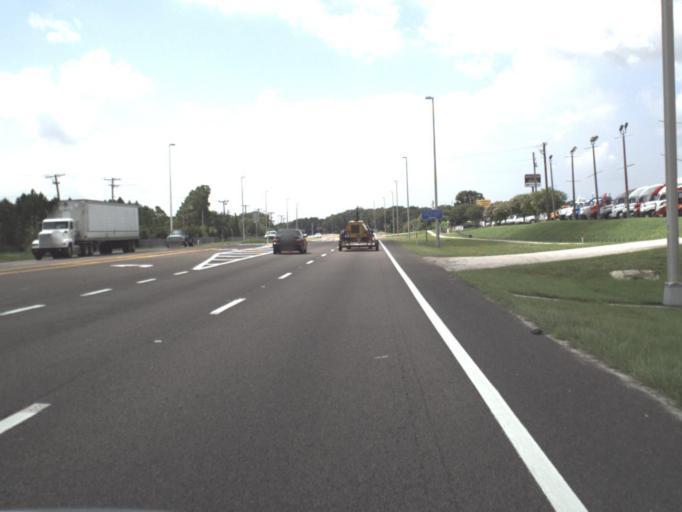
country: US
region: Florida
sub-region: Hillsborough County
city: Temple Terrace
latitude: 28.0180
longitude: -82.3526
